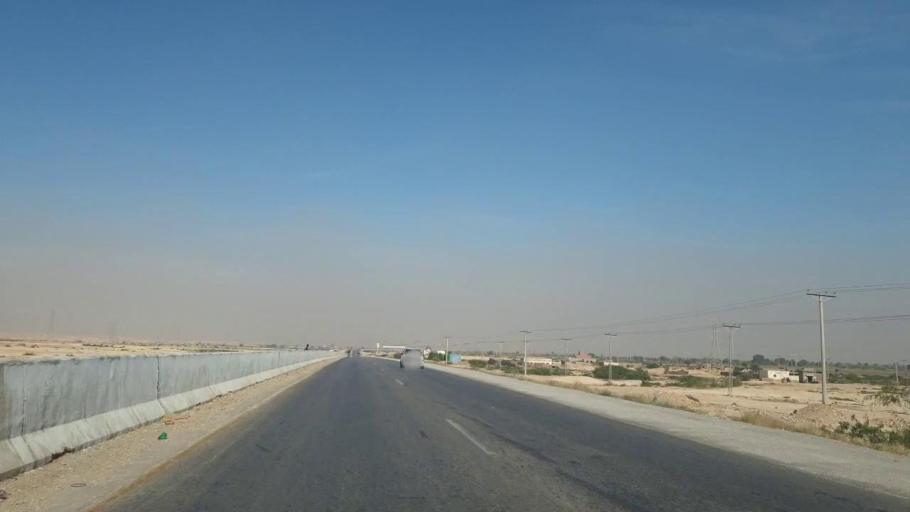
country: PK
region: Sindh
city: Jamshoro
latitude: 25.5078
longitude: 68.2732
